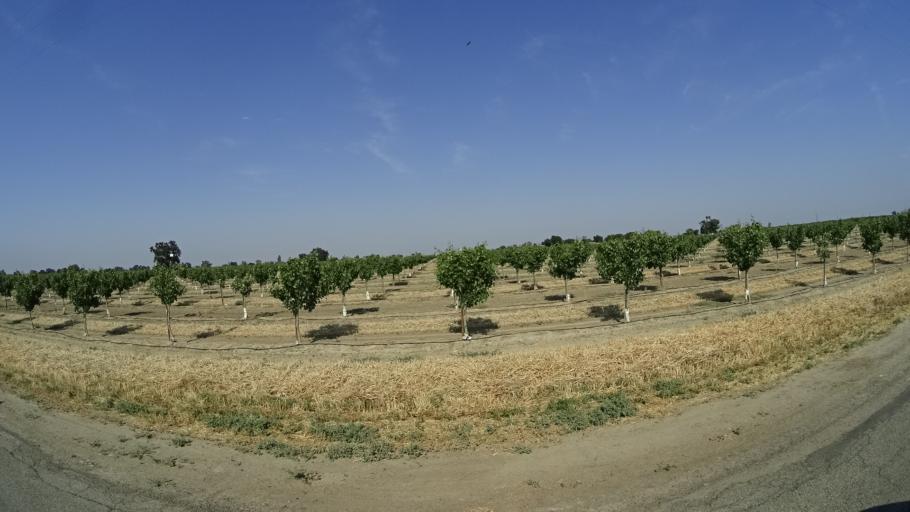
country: US
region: California
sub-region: Fresno County
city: Riverdale
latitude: 36.3563
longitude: -119.8430
